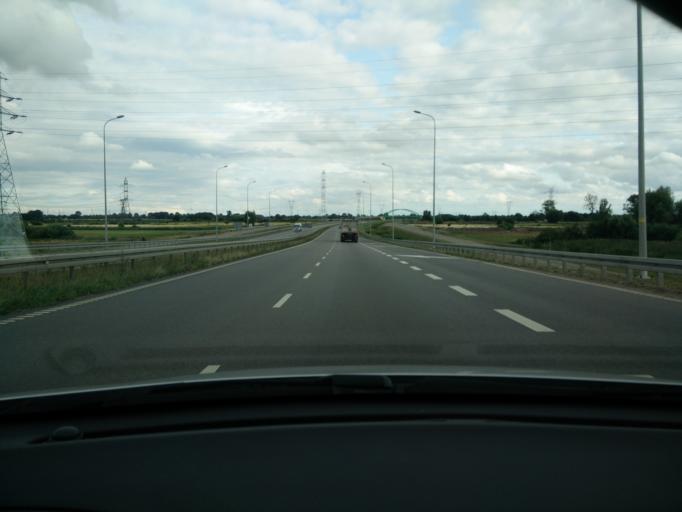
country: PL
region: Pomeranian Voivodeship
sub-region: Gdansk
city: Gdansk
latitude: 54.3411
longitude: 18.6986
